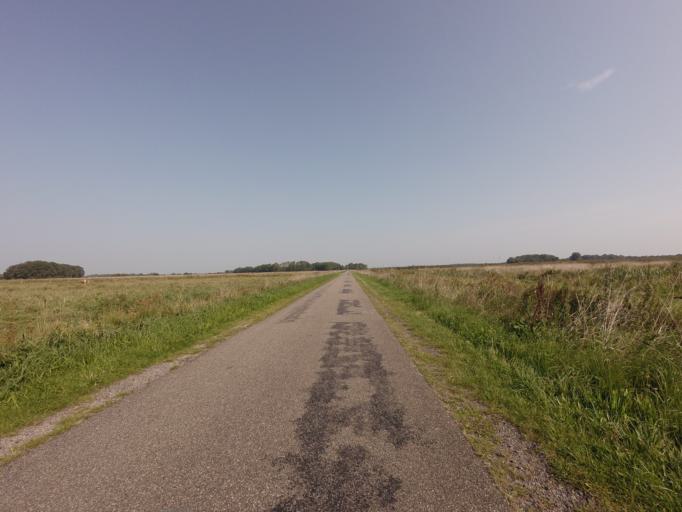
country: NL
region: Groningen
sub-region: Gemeente Groningen
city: Groningen
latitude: 53.1487
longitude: 6.5291
